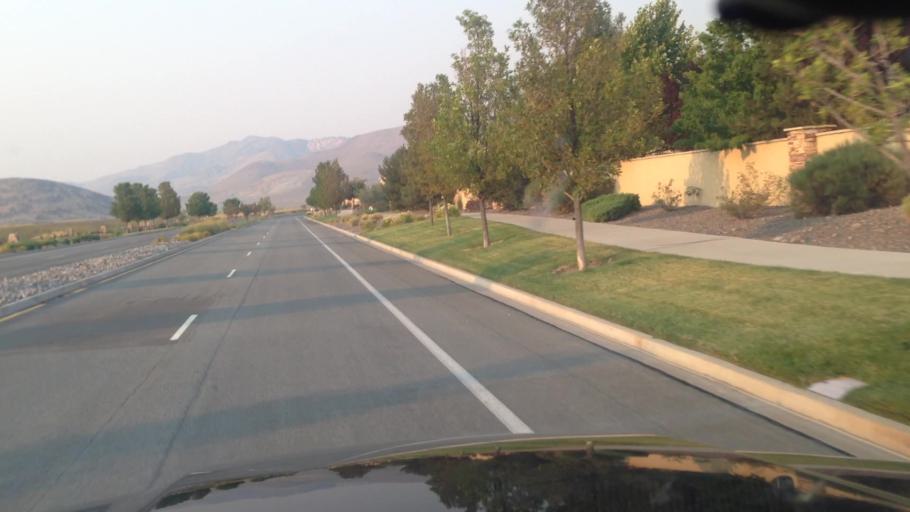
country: US
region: Nevada
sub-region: Washoe County
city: Sparks
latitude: 39.4497
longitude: -119.7399
